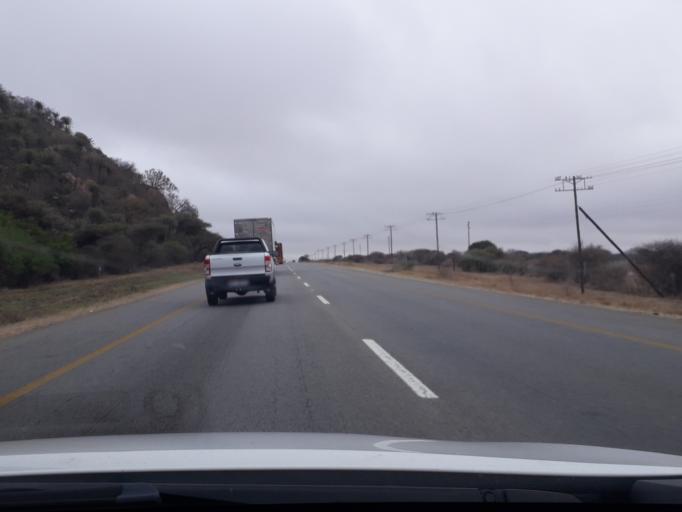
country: ZA
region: Limpopo
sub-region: Capricorn District Municipality
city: Mankoeng
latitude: -23.5263
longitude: 29.7058
